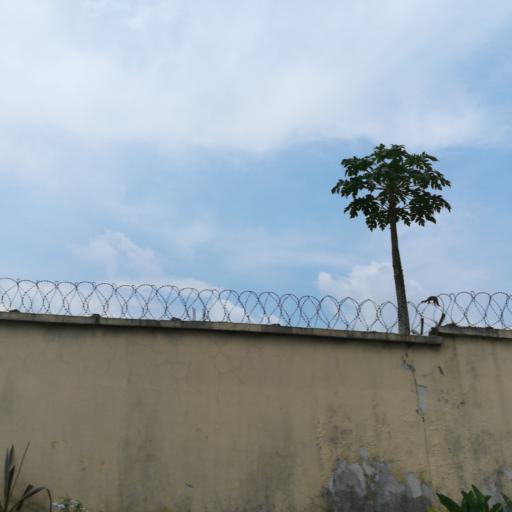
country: NG
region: Rivers
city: Port Harcourt
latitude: 4.8519
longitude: 7.0177
